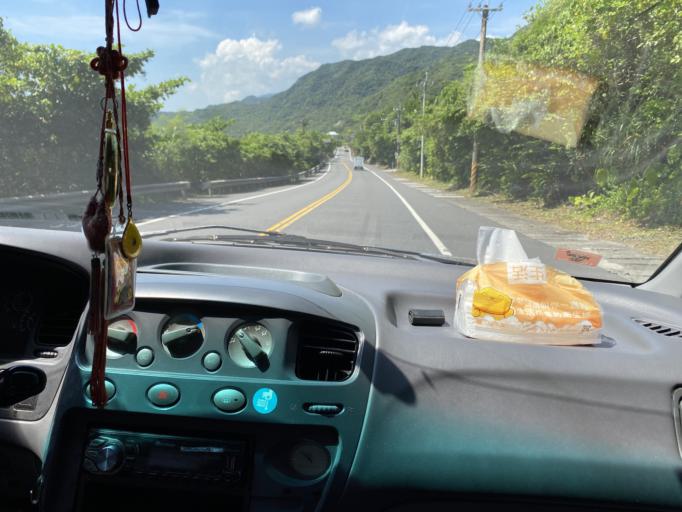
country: TW
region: Taiwan
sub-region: Keelung
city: Keelung
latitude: 24.9737
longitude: 121.9334
